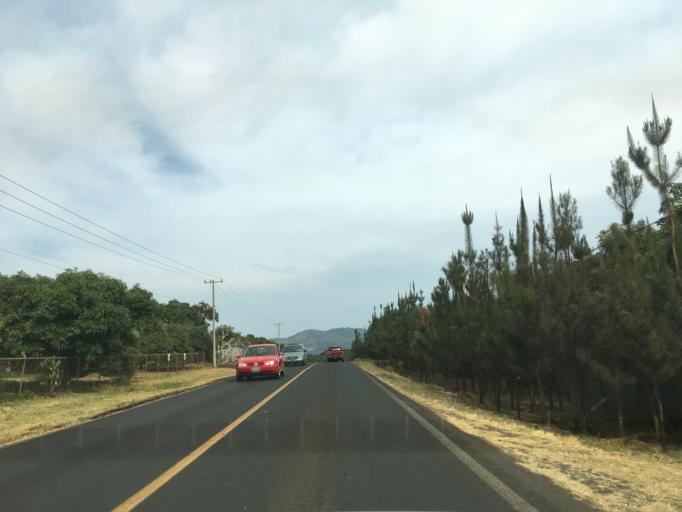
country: MX
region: Michoacan
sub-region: Uruapan
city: Uruapan
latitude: 19.3846
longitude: -102.0939
